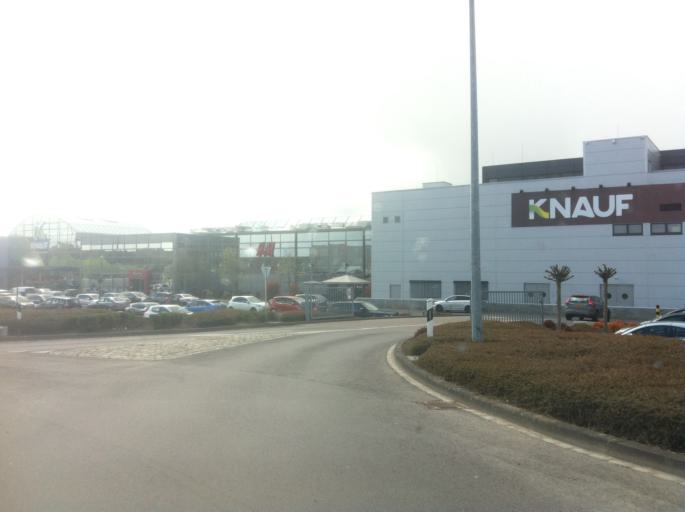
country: LU
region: Diekirch
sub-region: Canton de Wiltz
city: Winseler
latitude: 49.9644
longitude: 5.8584
